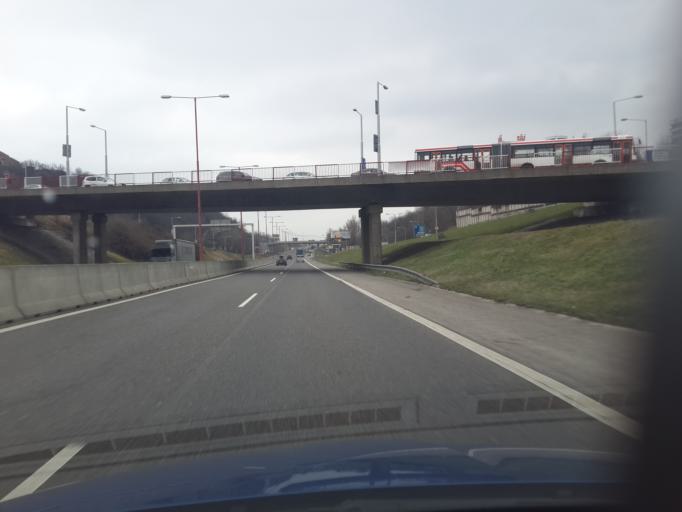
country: SK
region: Bratislavsky
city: Bratislava
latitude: 48.1545
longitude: 17.0763
